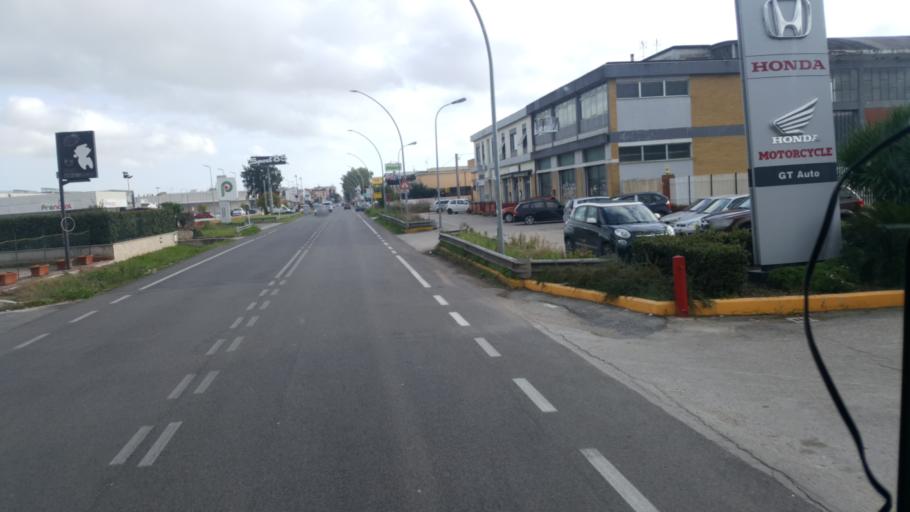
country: IT
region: Latium
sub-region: Provincia di Latina
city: Latina
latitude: 41.4763
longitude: 12.8790
